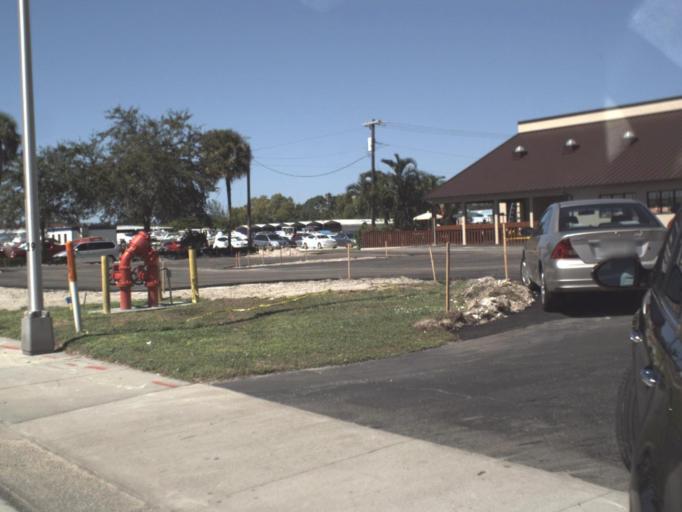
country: US
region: Florida
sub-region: Collier County
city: Naples
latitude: 26.1385
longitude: -81.7773
